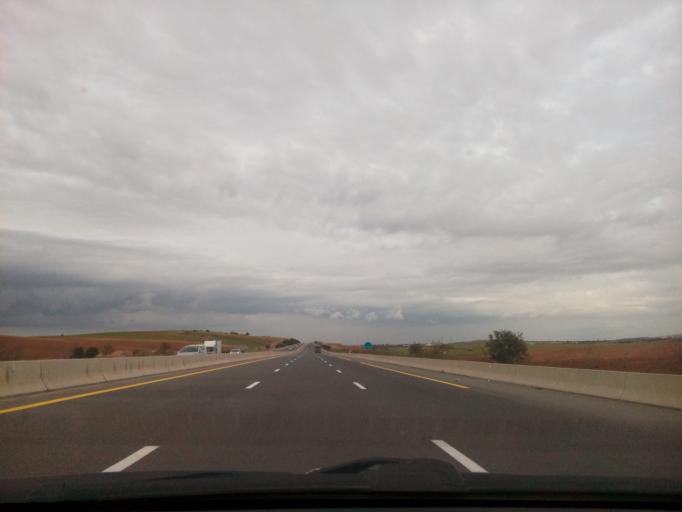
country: DZ
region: Mascara
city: Sig
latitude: 35.5033
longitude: -0.3744
